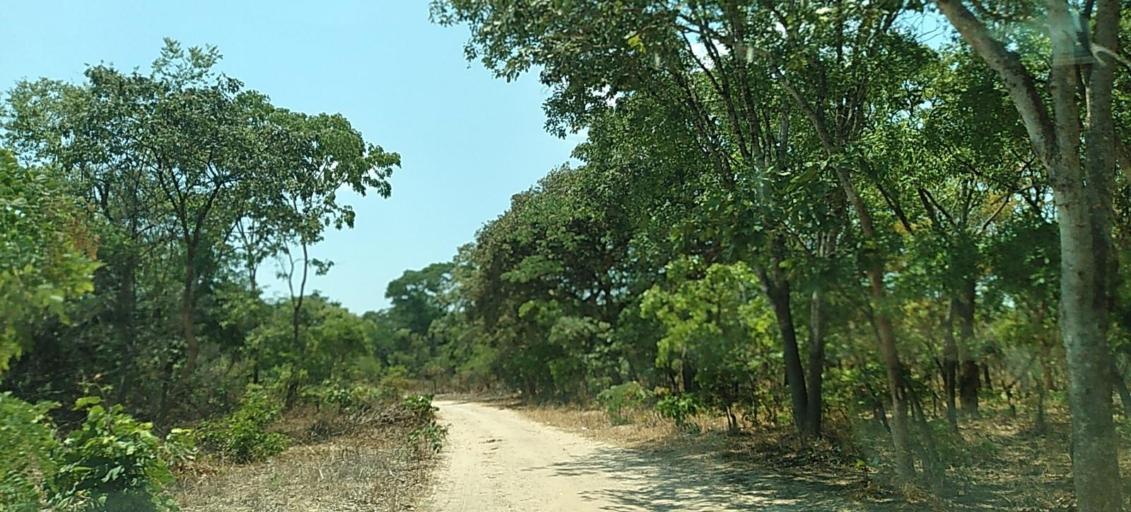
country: ZM
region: Central
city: Kapiri Mposhi
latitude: -13.6686
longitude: 28.4936
